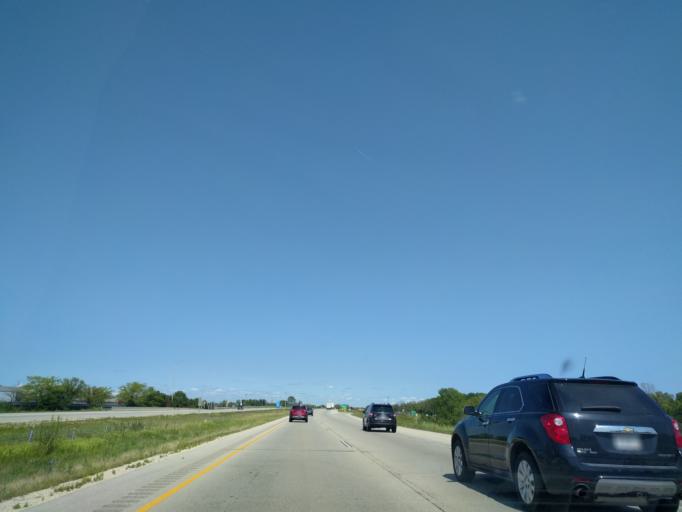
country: US
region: Wisconsin
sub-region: Milwaukee County
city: Bayside
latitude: 43.2171
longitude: -87.9212
